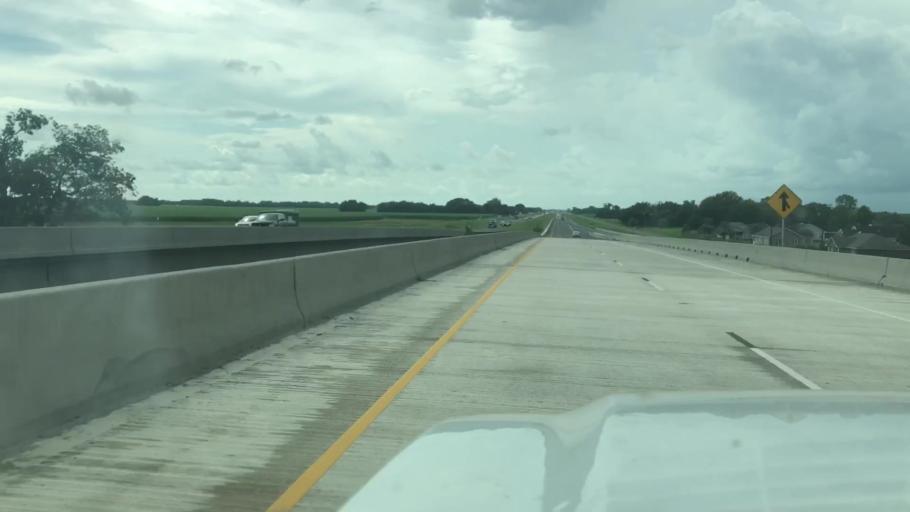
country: US
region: Louisiana
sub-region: Iberia Parish
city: Jeanerette
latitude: 29.8672
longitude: -91.6347
